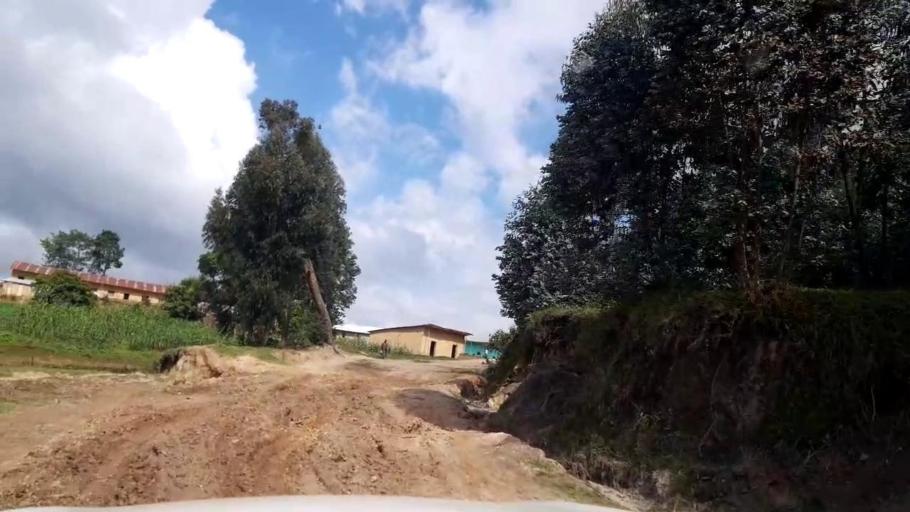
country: RW
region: Western Province
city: Kibuye
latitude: -1.8812
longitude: 29.4779
